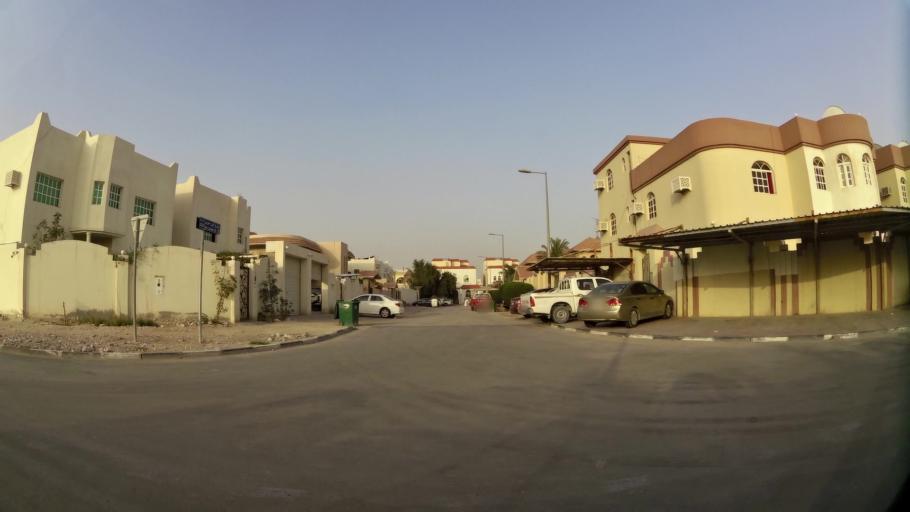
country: QA
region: Baladiyat ar Rayyan
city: Ar Rayyan
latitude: 25.2383
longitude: 51.4478
